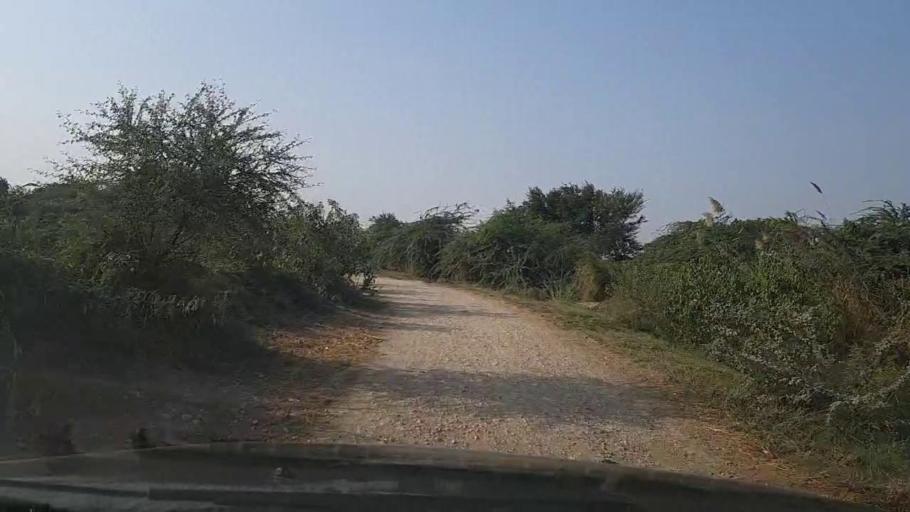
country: PK
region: Sindh
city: Mirpur Sakro
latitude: 24.6385
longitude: 67.7496
